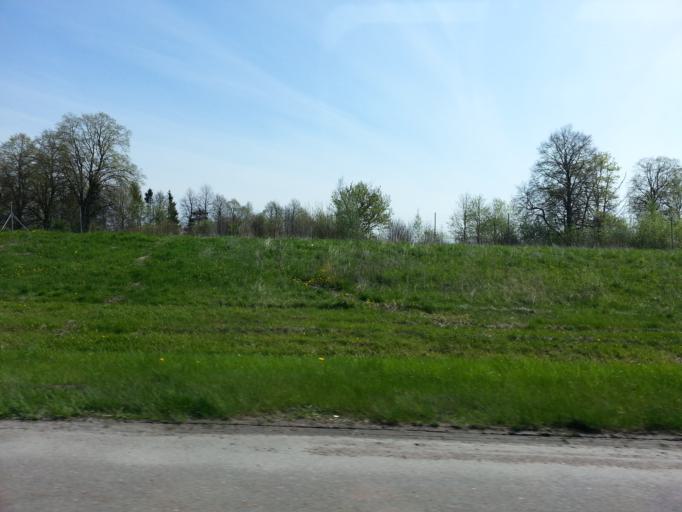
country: LT
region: Vilnius County
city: Ukmerge
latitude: 55.1488
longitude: 24.8254
